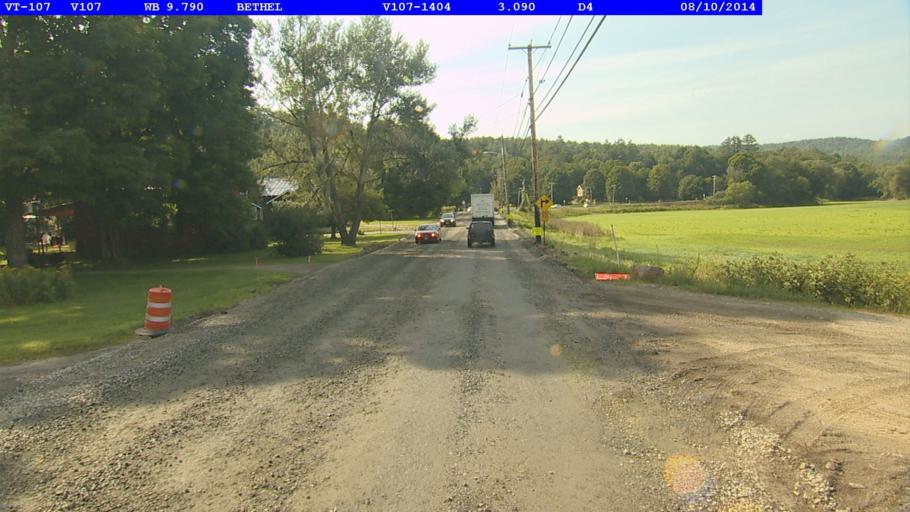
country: US
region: Vermont
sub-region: Orange County
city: Randolph
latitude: 43.8244
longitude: -72.6319
